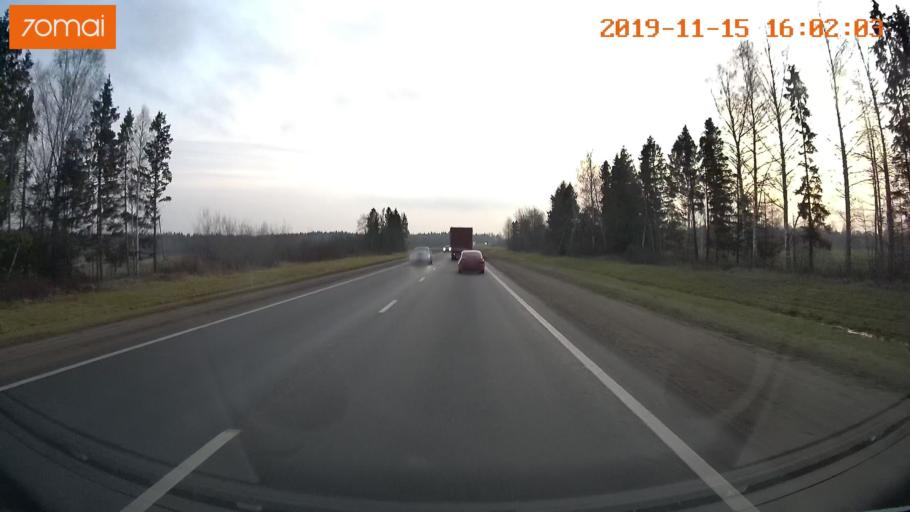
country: RU
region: Jaroslavl
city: Yaroslavl
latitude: 57.7757
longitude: 39.9272
